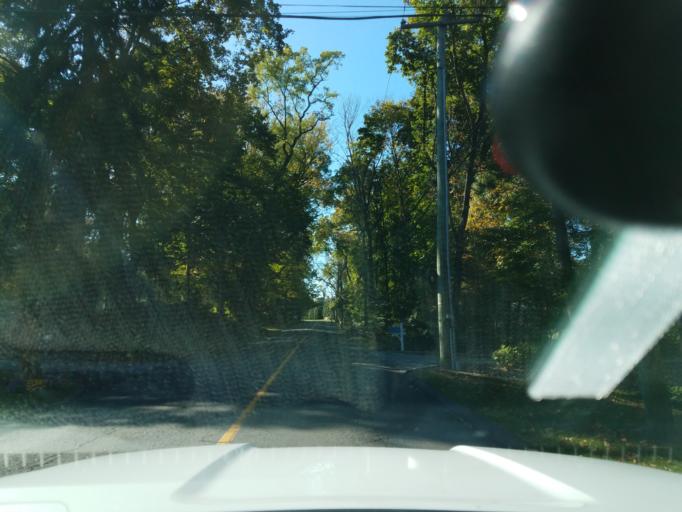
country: US
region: Connecticut
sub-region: Fairfield County
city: Cos Cob
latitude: 41.0414
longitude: -73.6166
